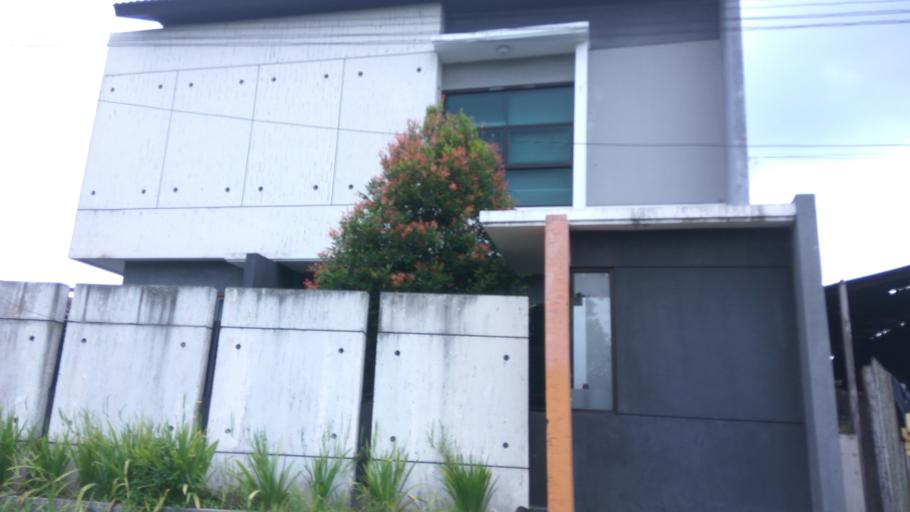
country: ID
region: Daerah Istimewa Yogyakarta
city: Melati
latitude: -7.7229
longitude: 110.4039
